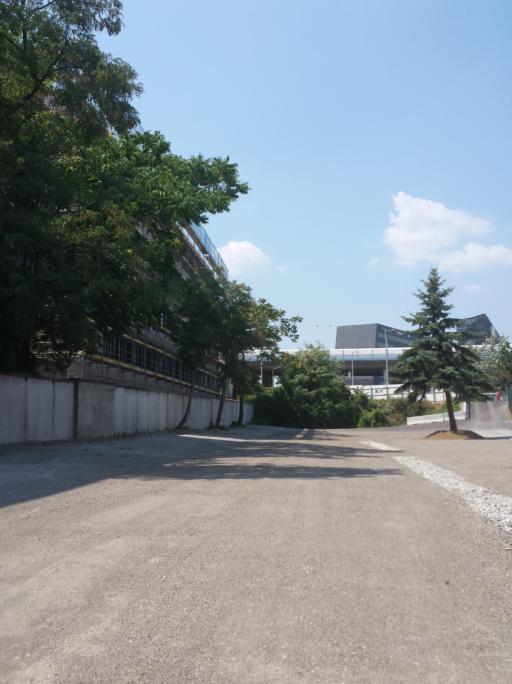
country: AT
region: Vienna
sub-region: Wien Stadt
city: Vienna
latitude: 48.1847
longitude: 16.4079
